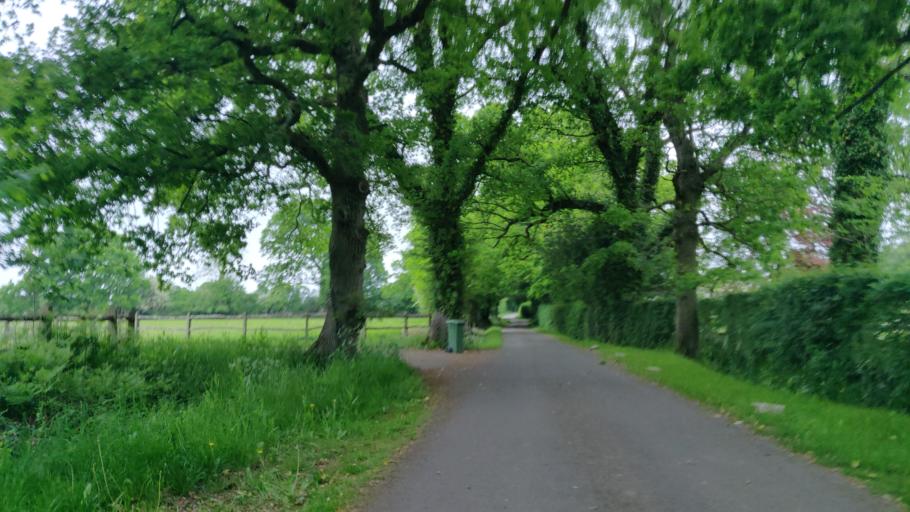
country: GB
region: England
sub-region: West Sussex
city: Southwater
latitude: 51.0186
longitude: -0.3317
